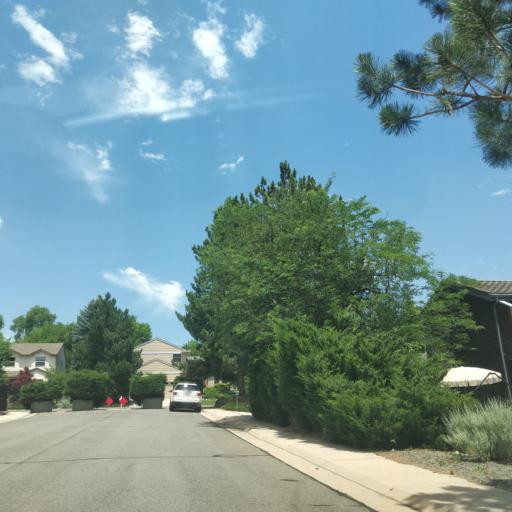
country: US
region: Colorado
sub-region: Jefferson County
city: Lakewood
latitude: 39.6746
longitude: -105.0955
